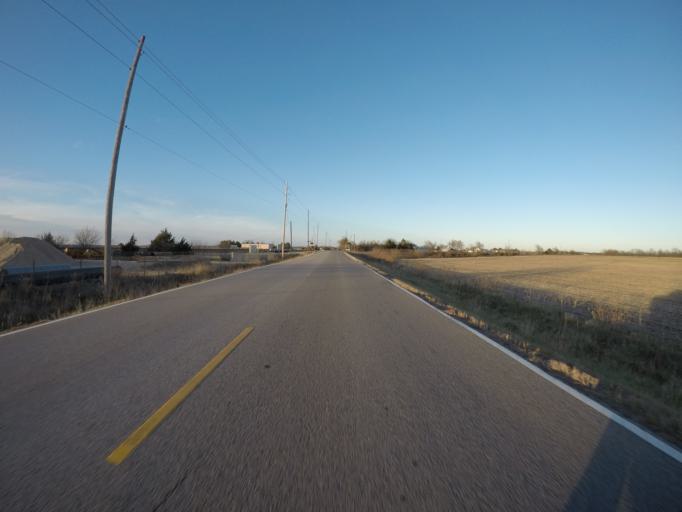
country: US
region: Kansas
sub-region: Harvey County
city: North Newton
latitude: 38.0611
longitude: -97.3184
